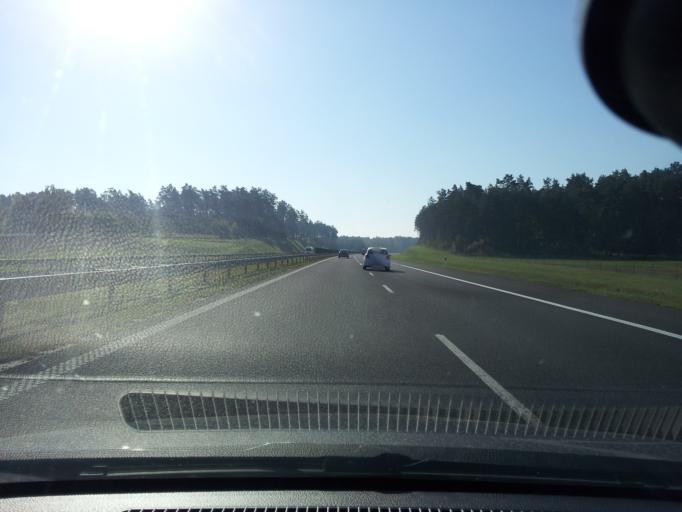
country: PL
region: Pomeranian Voivodeship
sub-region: Powiat starogardzki
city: Smetowo Graniczne
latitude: 53.6752
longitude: 18.6370
